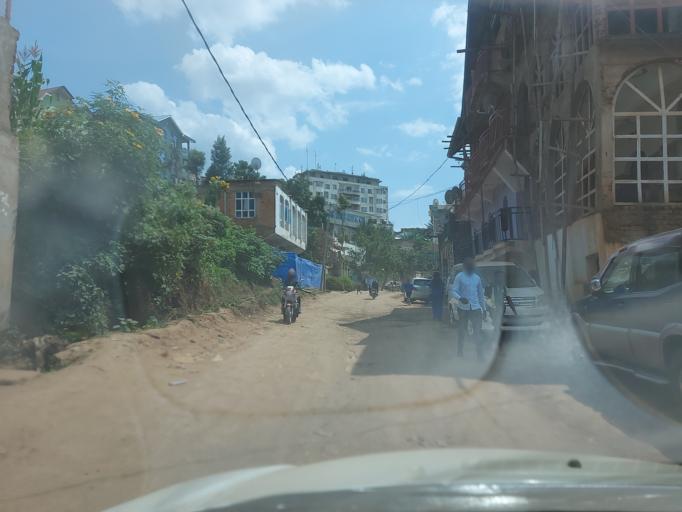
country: CD
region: South Kivu
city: Bukavu
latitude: -2.4999
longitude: 28.8565
